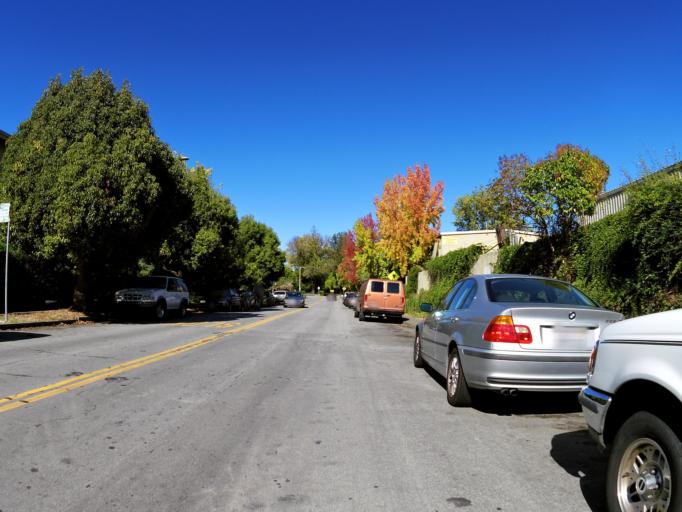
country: US
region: California
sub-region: Marin County
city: Kentfield
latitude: 37.9528
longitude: -122.5509
